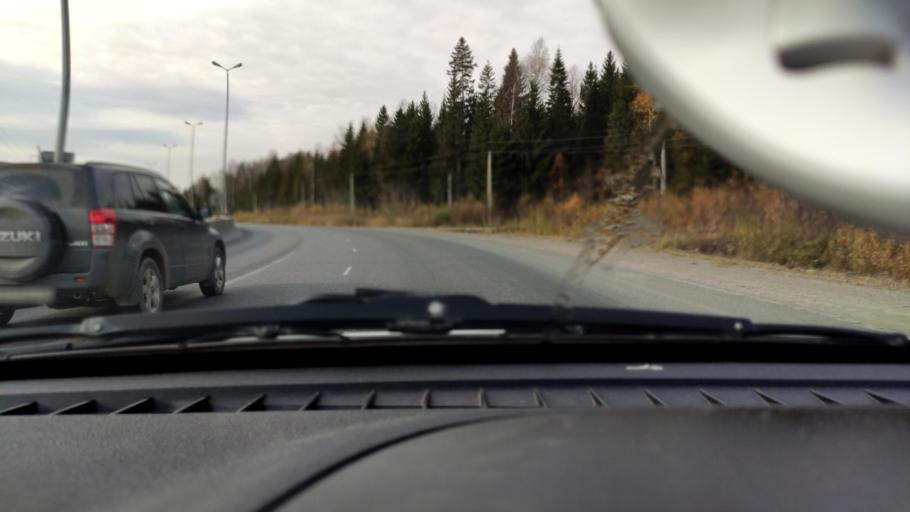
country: RU
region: Perm
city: Kondratovo
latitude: 58.0584
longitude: 56.0815
